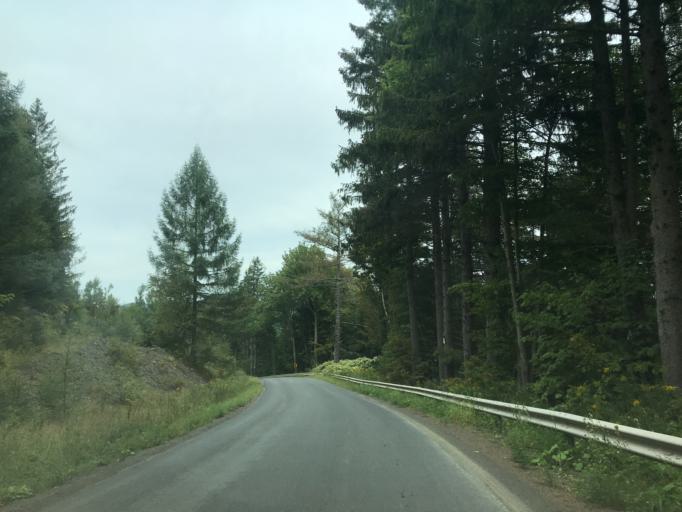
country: US
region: New York
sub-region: Otsego County
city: Worcester
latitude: 42.5900
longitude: -74.7001
